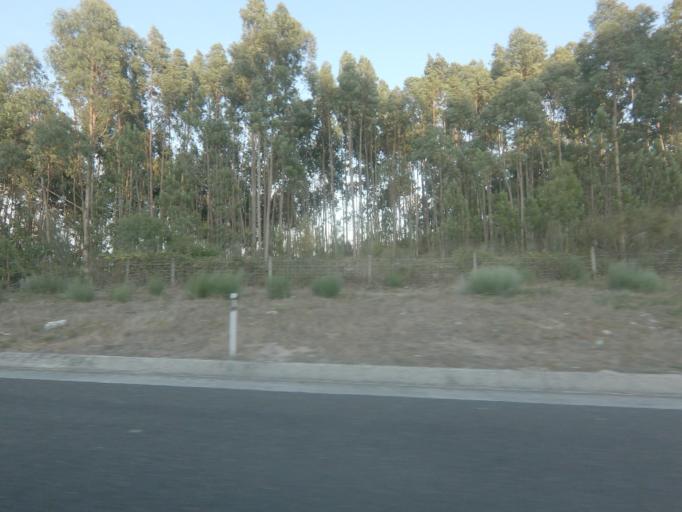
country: PT
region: Leiria
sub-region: Leiria
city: Santa Catarina da Serra
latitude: 39.6755
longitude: -8.6842
